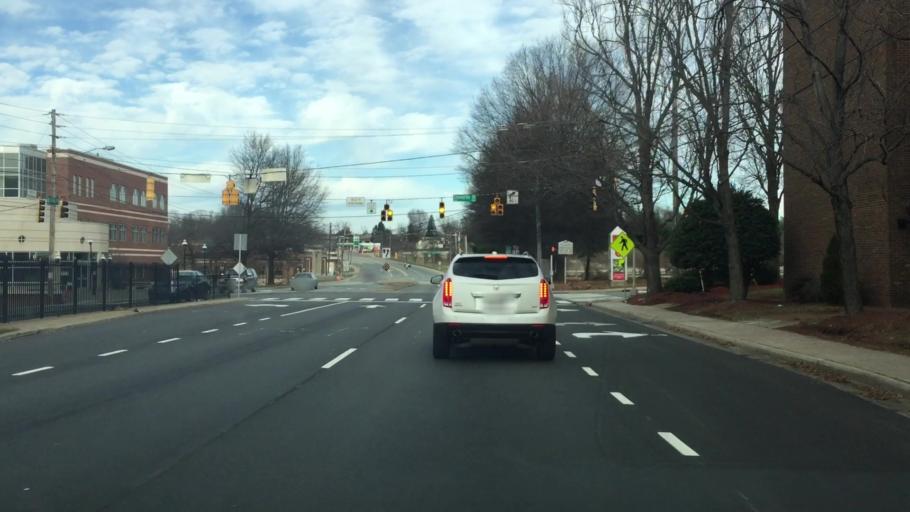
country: US
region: North Carolina
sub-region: Forsyth County
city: Winston-Salem
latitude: 36.0919
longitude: -80.2276
